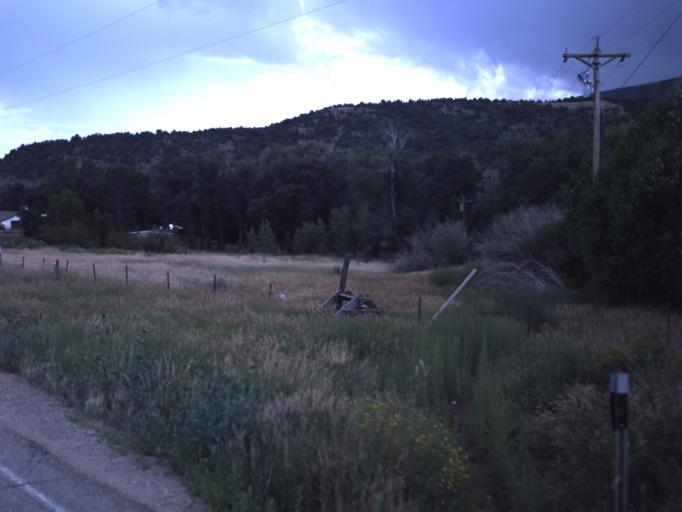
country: US
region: Utah
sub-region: Duchesne County
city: Duchesne
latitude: 40.4002
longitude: -110.7598
